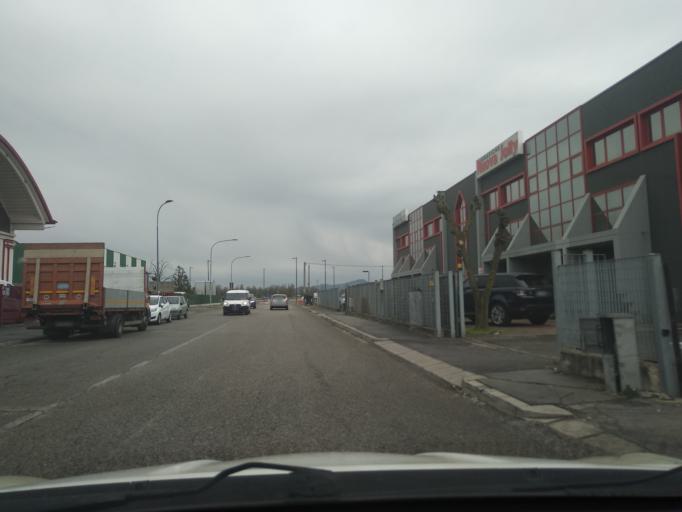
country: IT
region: Veneto
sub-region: Provincia di Padova
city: Rubano
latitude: 45.4174
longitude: 11.7935
